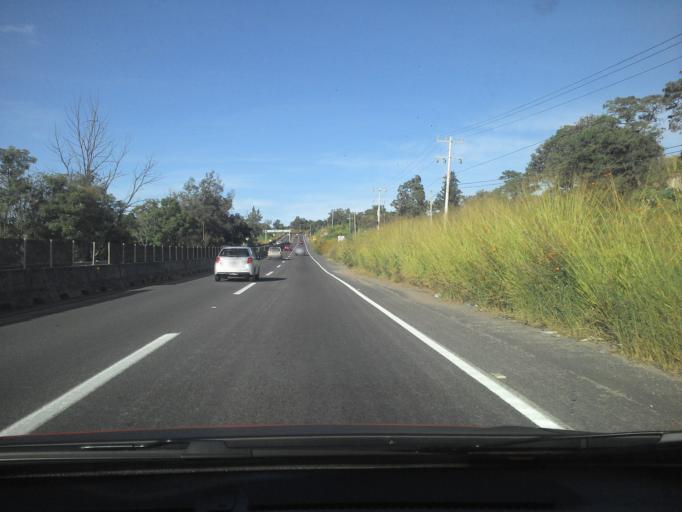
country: MX
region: Jalisco
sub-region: Tala
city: Los Ruisenores
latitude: 20.7229
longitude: -103.6222
